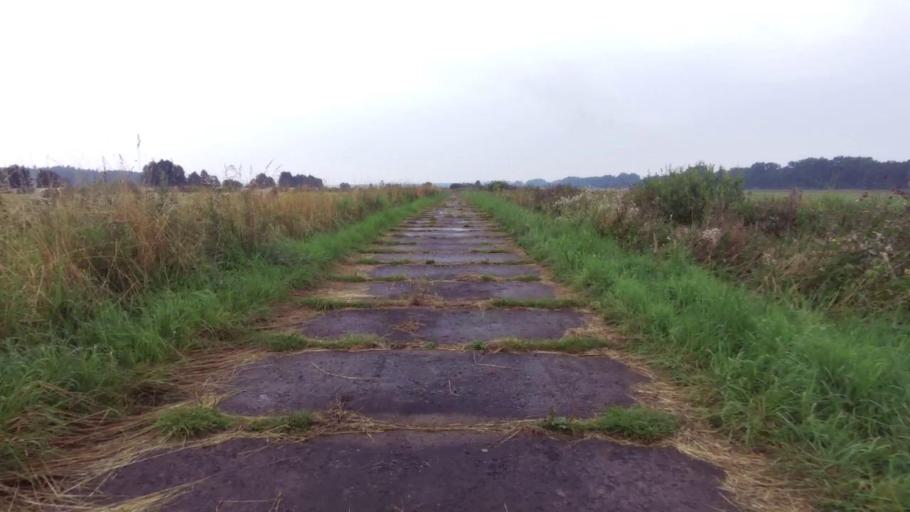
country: PL
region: West Pomeranian Voivodeship
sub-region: Powiat choszczenski
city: Choszczno
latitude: 53.2477
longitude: 15.4202
